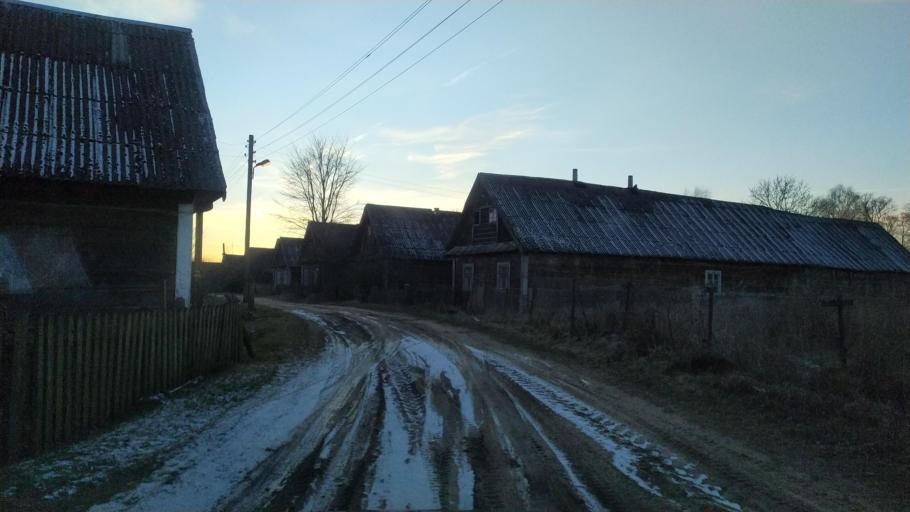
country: BY
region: Brest
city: Pruzhany
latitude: 52.5509
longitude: 24.2525
